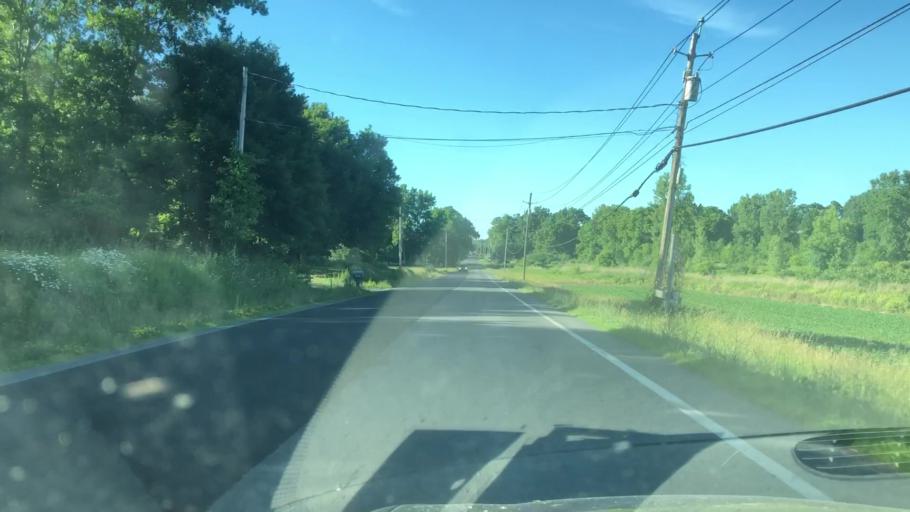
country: US
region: New York
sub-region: Wayne County
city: Macedon
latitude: 43.1129
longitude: -77.3208
